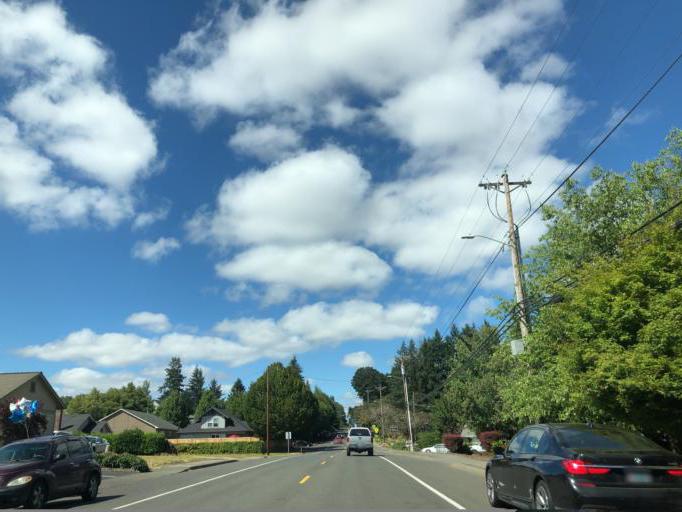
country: US
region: Oregon
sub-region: Marion County
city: Silverton
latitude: 45.0112
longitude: -122.7736
